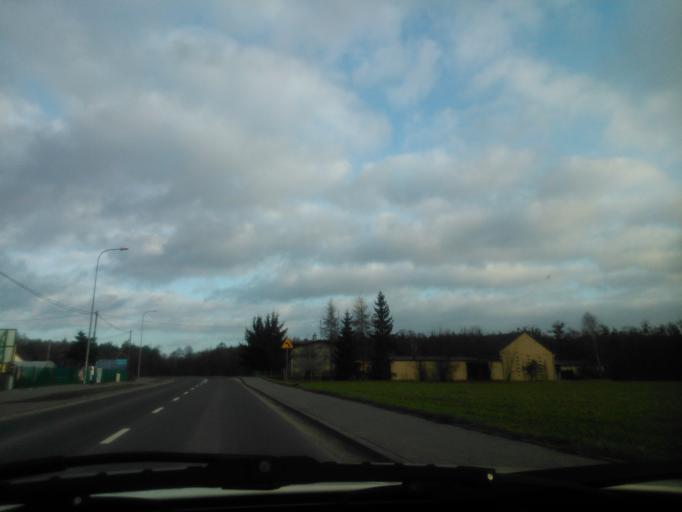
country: PL
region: Kujawsko-Pomorskie
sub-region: Powiat golubsko-dobrzynski
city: Golub-Dobrzyn
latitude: 53.1187
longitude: 19.0667
